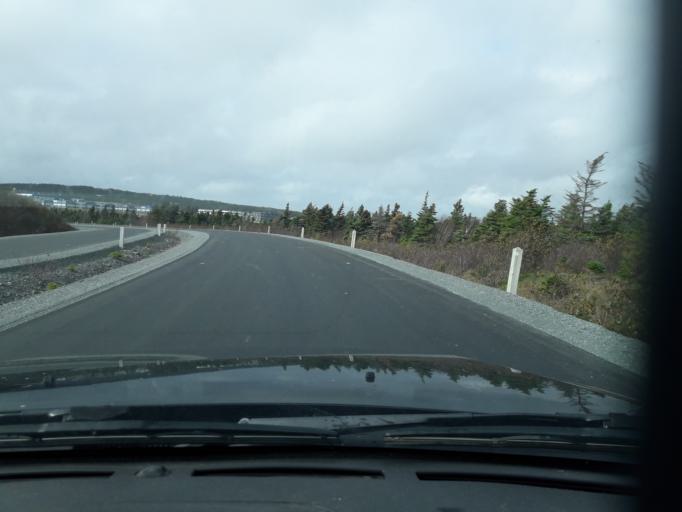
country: CA
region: Newfoundland and Labrador
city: Mount Pearl
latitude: 47.5553
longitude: -52.7717
